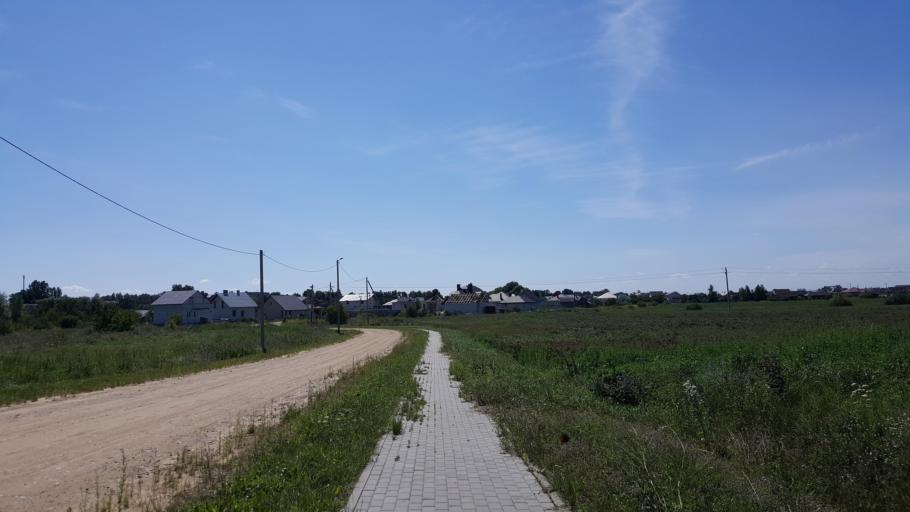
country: BY
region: Brest
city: Charnawchytsy
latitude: 52.2180
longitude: 23.7365
